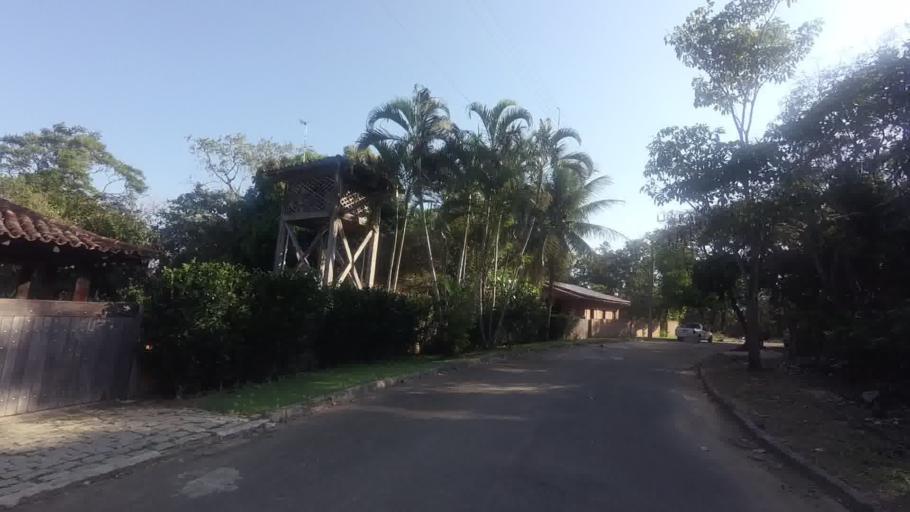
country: BR
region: Espirito Santo
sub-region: Guarapari
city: Guarapari
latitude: -20.7291
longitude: -40.5365
